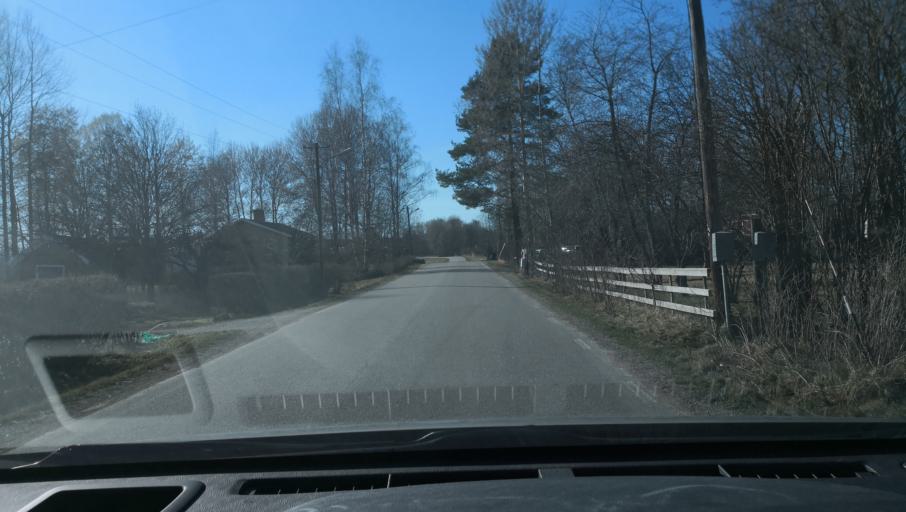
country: SE
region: Vaestmanland
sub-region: Sala Kommun
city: Sala
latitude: 60.0843
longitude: 16.5339
